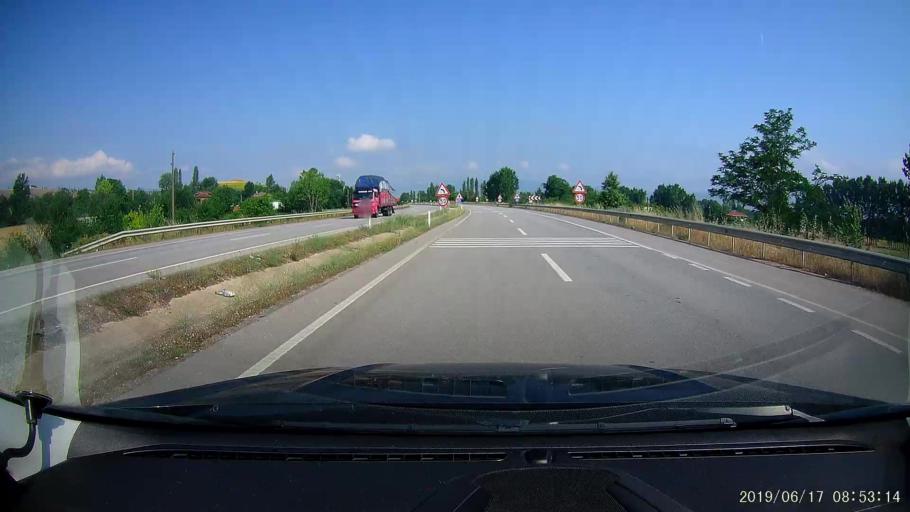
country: TR
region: Tokat
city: Erbaa
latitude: 40.7077
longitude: 36.4847
